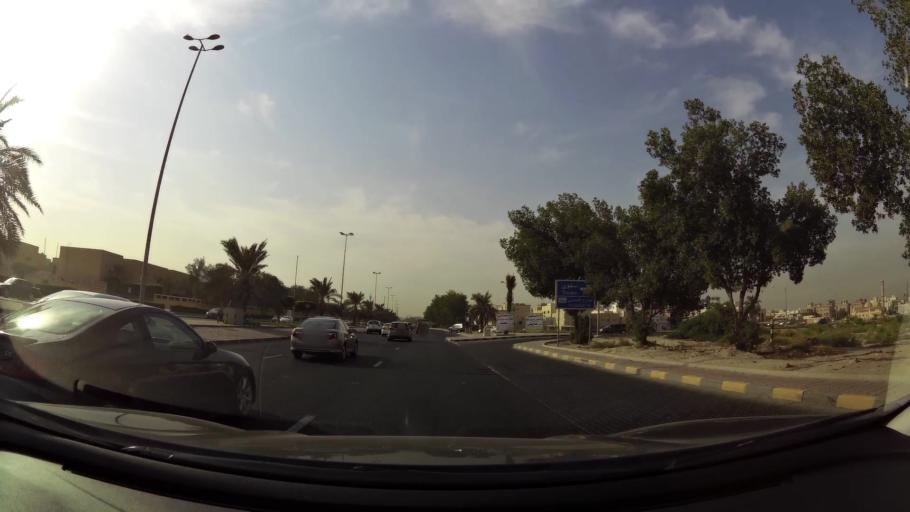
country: KW
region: Muhafazat Hawalli
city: Salwa
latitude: 29.3051
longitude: 48.0855
